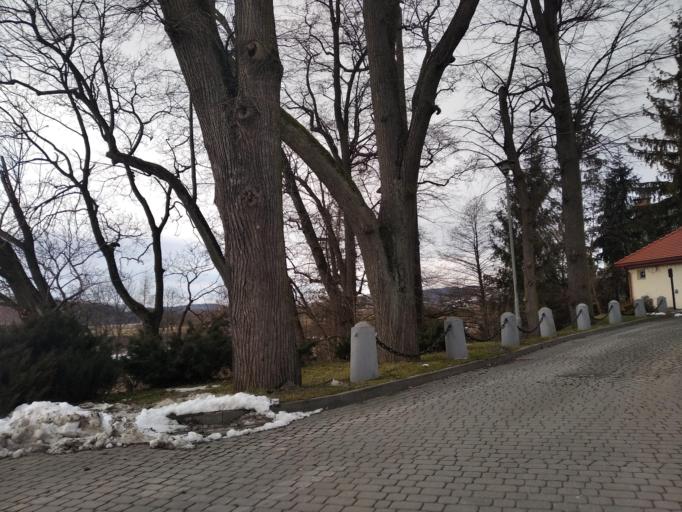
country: PL
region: Subcarpathian Voivodeship
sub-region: Powiat przemyski
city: Dubiecko
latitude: 49.8218
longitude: 22.3931
